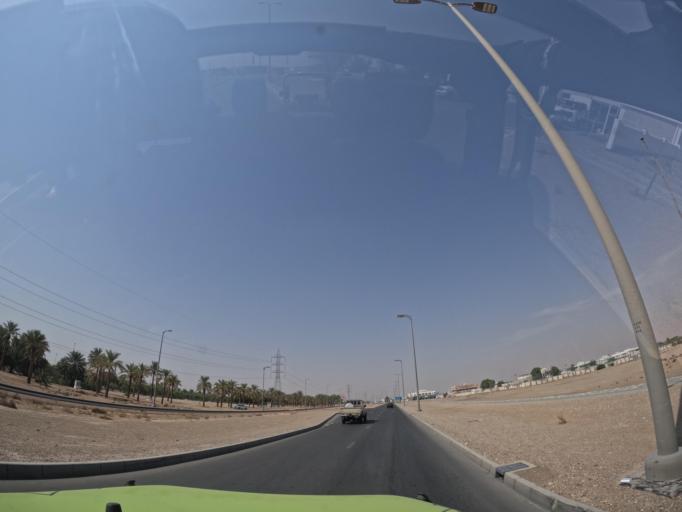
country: AE
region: Abu Dhabi
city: Al Ain
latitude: 24.2254
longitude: 55.5572
